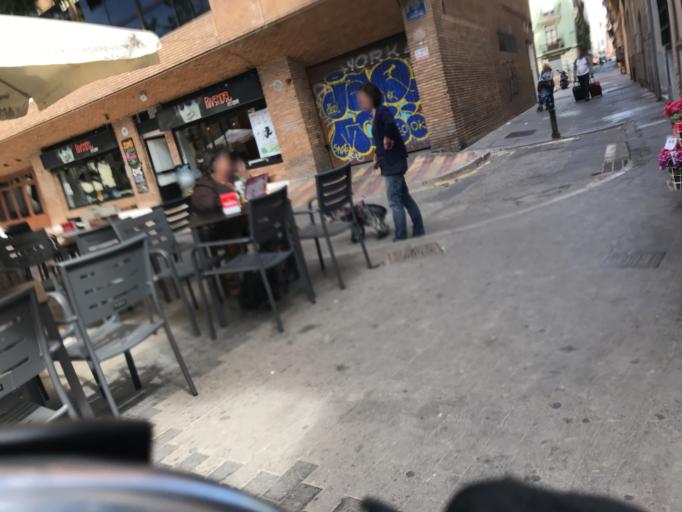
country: ES
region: Valencia
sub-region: Provincia de Valencia
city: Valencia
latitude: 39.4708
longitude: -0.3814
